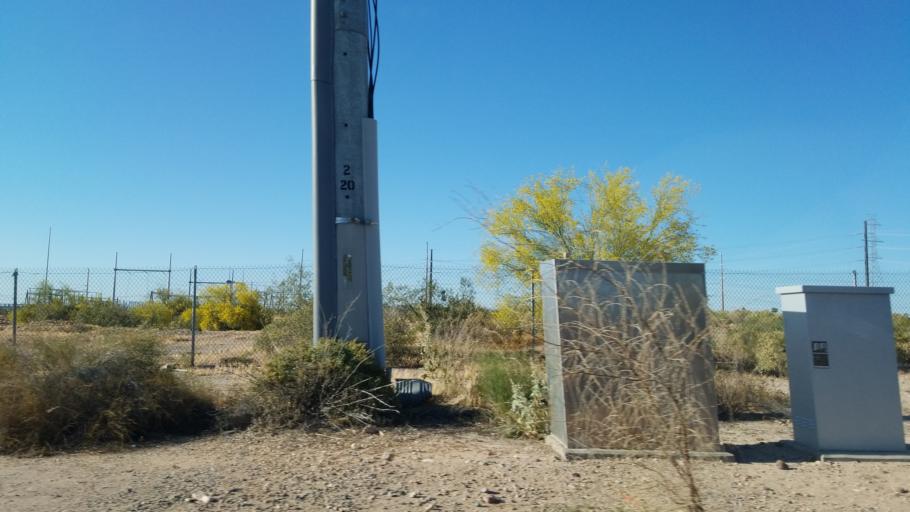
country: US
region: Arizona
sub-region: Maricopa County
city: Youngtown
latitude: 33.5655
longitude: -112.3047
